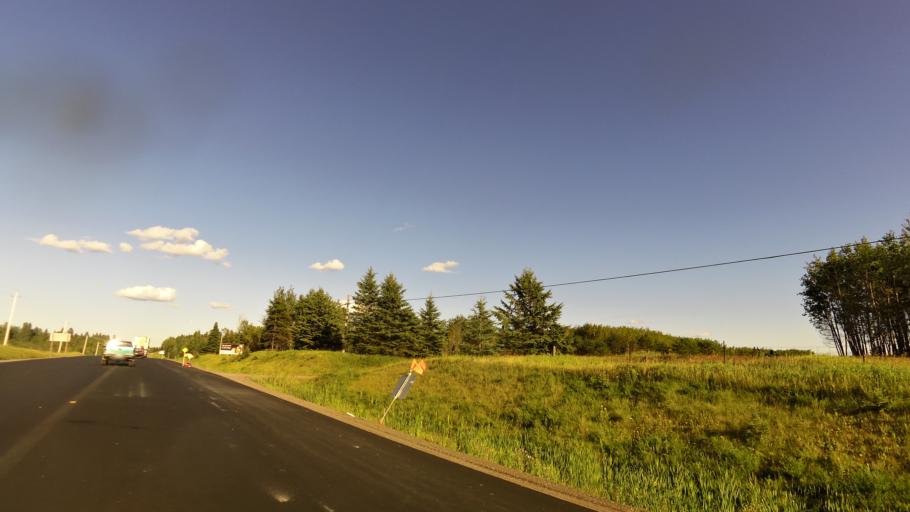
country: CA
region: Ontario
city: Dryden
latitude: 49.8151
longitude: -92.8902
